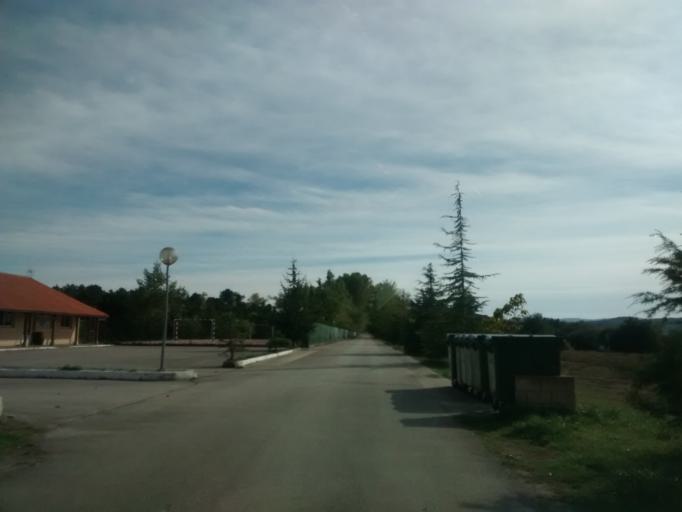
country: ES
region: Castille and Leon
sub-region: Provincia de Burgos
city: Arija
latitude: 43.0002
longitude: -3.9450
